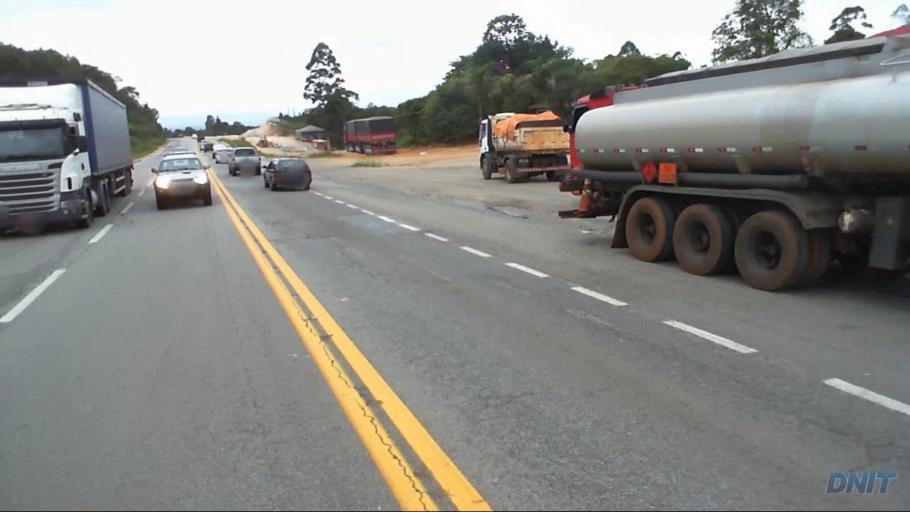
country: BR
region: Minas Gerais
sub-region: Caete
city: Caete
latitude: -19.7535
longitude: -43.5281
